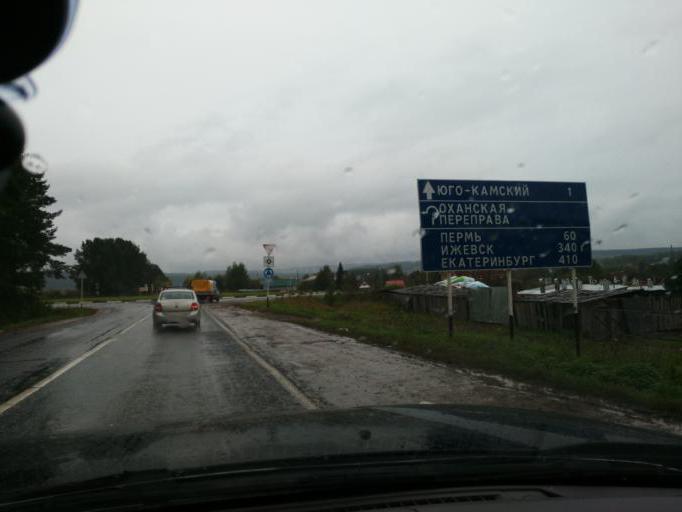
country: RU
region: Perm
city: Yugo-Kamskiy
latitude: 57.6868
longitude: 55.5677
